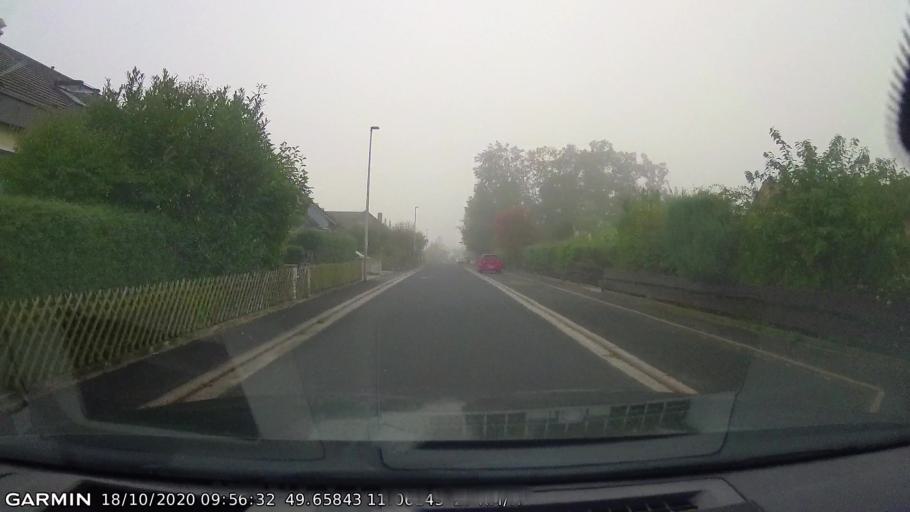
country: DE
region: Bavaria
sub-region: Upper Franconia
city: Poxdorf
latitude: 49.6582
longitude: 11.0609
